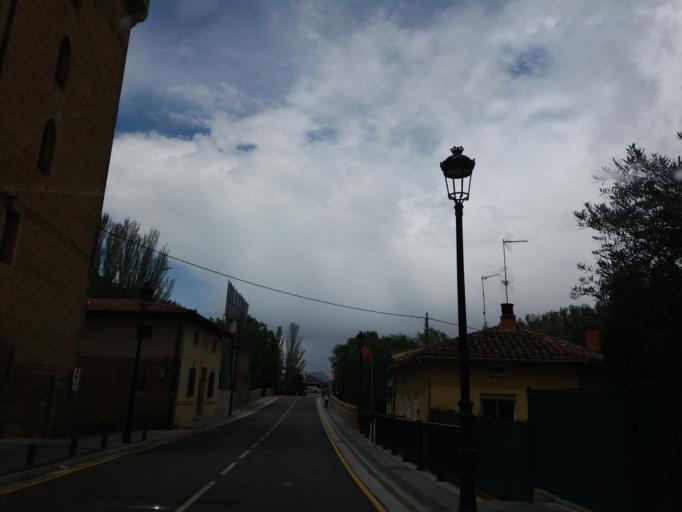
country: ES
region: La Rioja
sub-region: Provincia de La Rioja
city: Anguciana
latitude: 42.5751
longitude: -2.9036
